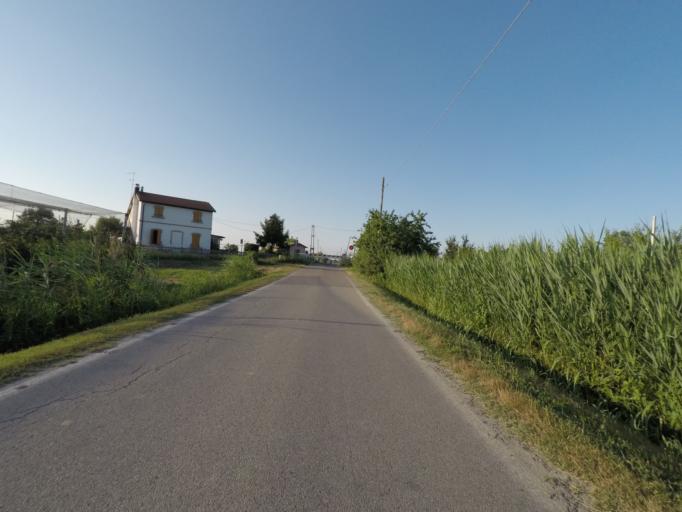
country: IT
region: Veneto
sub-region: Provincia di Rovigo
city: Costa di Rovigo
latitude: 45.0385
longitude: 11.6702
